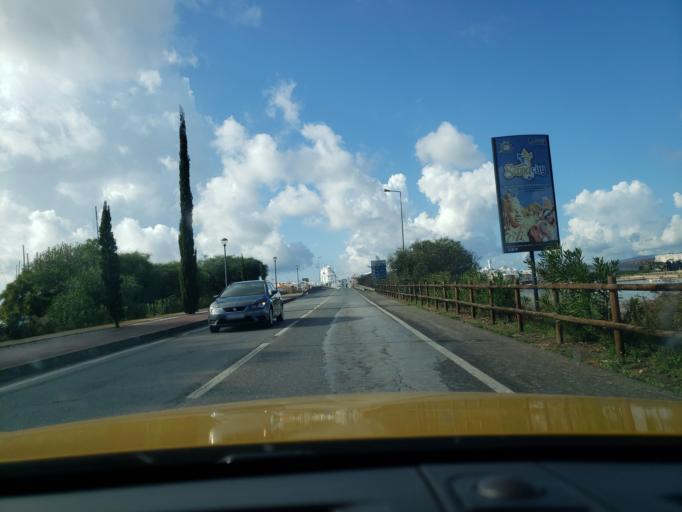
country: PT
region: Faro
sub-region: Portimao
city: Portimao
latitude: 37.1380
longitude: -8.5276
